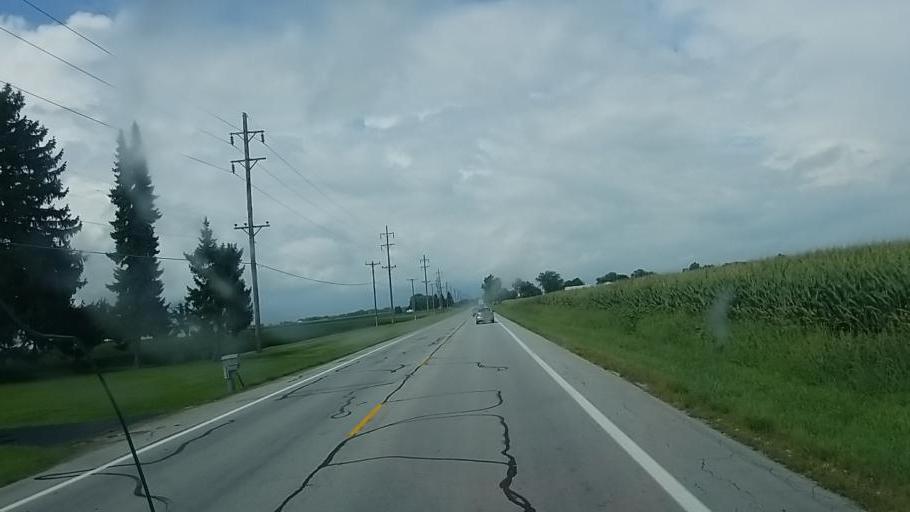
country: US
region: Ohio
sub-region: Logan County
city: West Liberty
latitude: 40.1872
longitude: -83.7423
